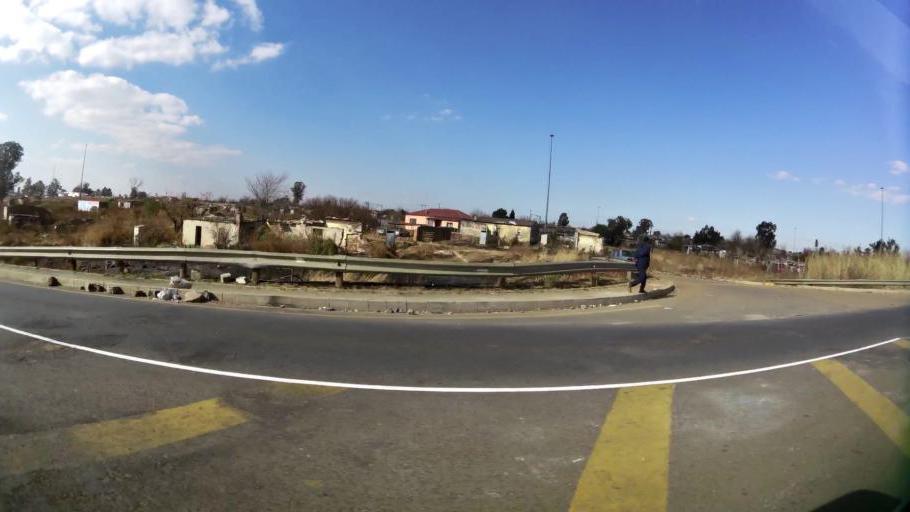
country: ZA
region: Gauteng
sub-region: City of Johannesburg Metropolitan Municipality
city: Soweto
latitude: -26.2657
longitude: 27.8895
